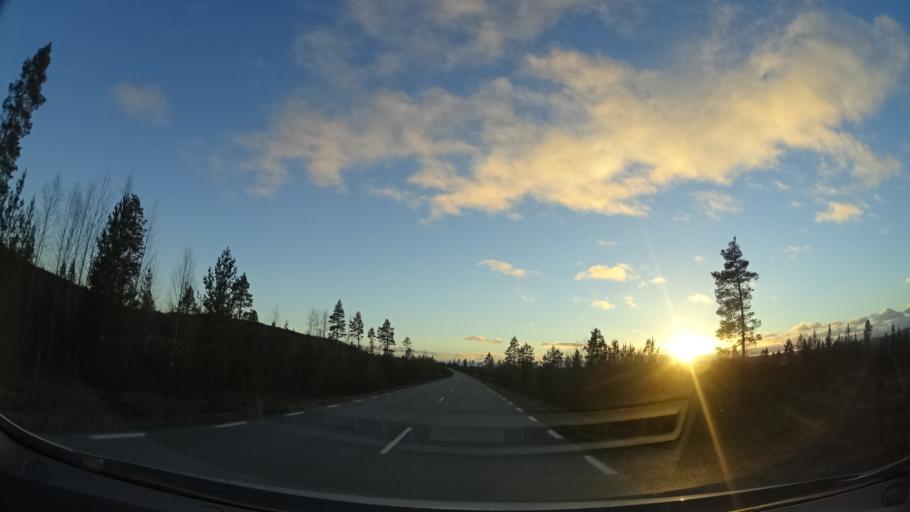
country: SE
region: Jaemtland
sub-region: Stroemsunds Kommun
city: Stroemsund
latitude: 63.9820
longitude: 15.4953
